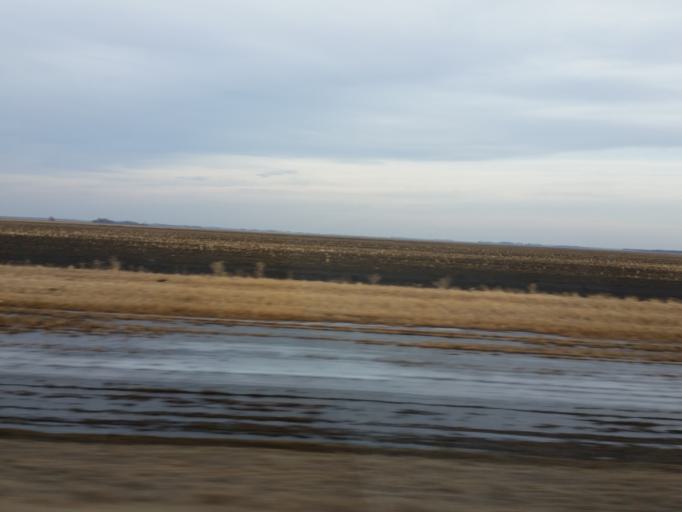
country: US
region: North Dakota
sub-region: Traill County
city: Hillsboro
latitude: 47.2796
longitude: -97.2177
